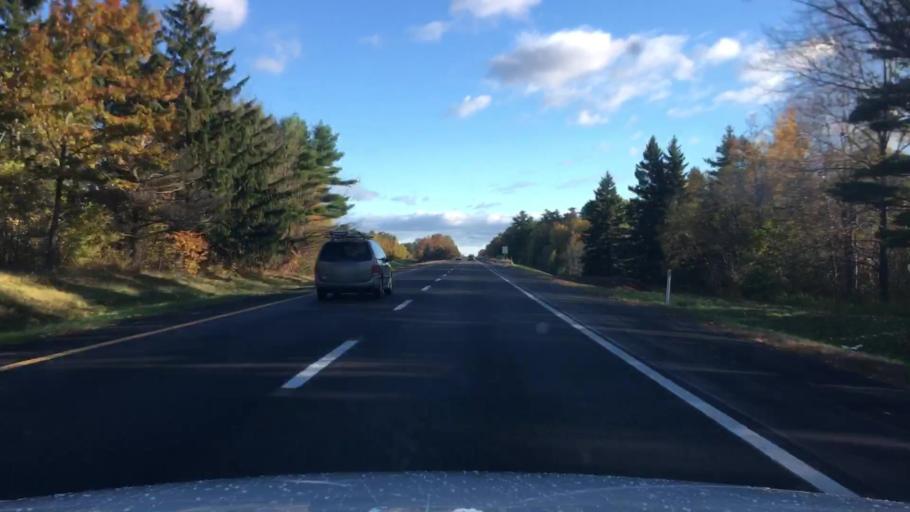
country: US
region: Maine
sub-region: Penobscot County
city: Veazie
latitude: 44.8376
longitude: -68.7368
